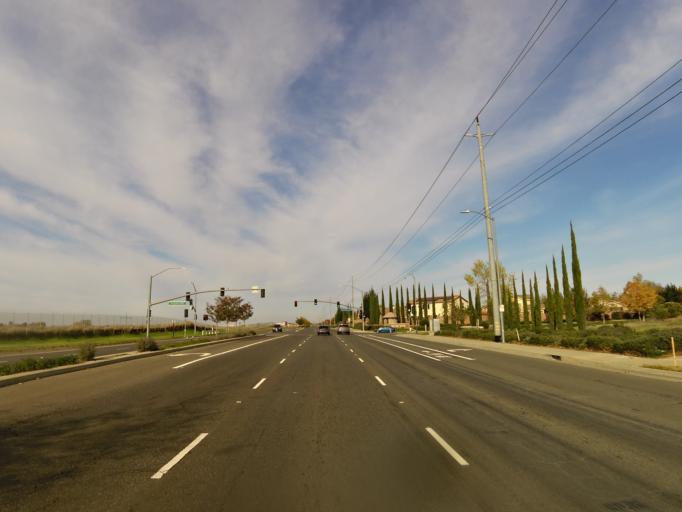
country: US
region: California
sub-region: Sacramento County
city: Rancho Cordova
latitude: 38.5475
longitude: -121.2428
